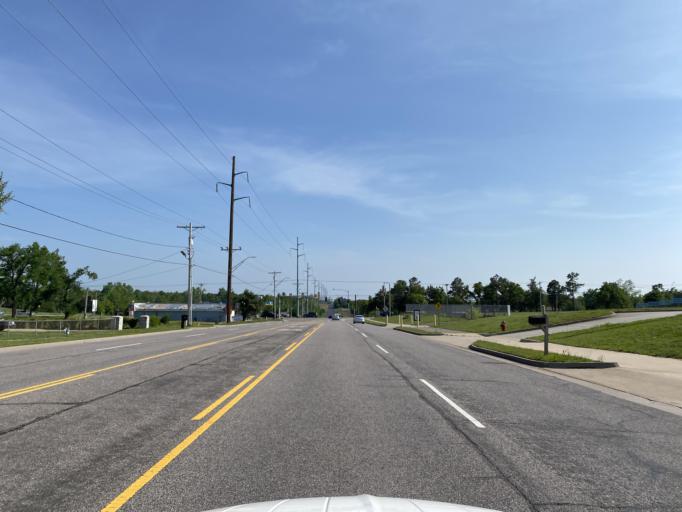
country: US
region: Oklahoma
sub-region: Oklahoma County
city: Midwest City
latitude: 35.4367
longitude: -97.3532
